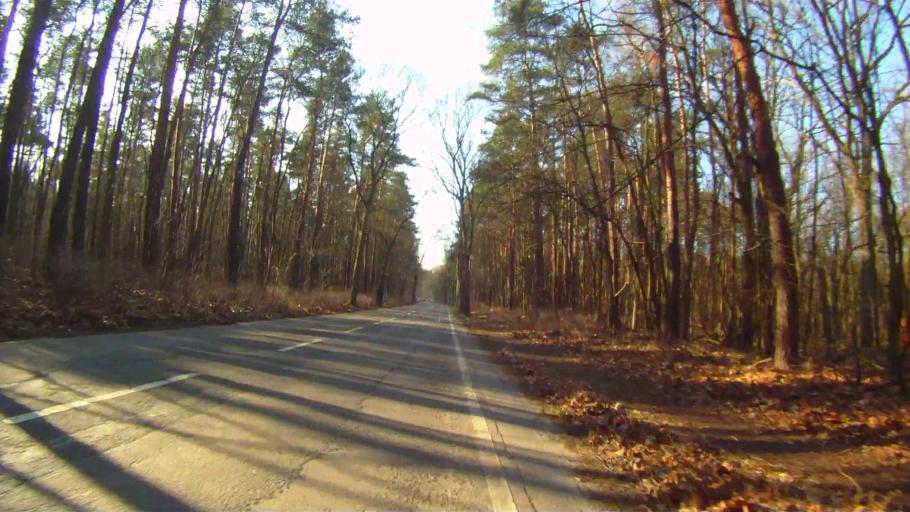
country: DE
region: Berlin
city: Rahnsdorf
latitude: 52.4538
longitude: 13.6999
